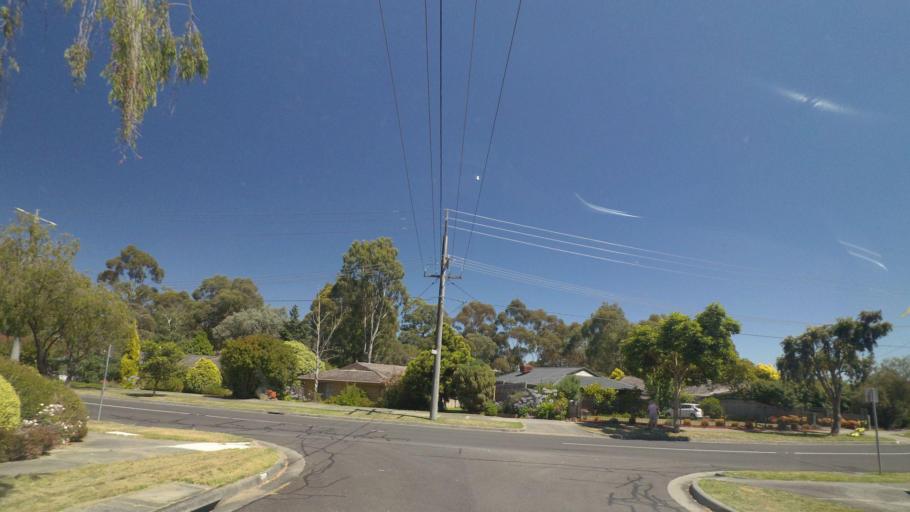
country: AU
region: Victoria
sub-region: Maroondah
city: Warranwood
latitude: -37.7933
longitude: 145.2392
